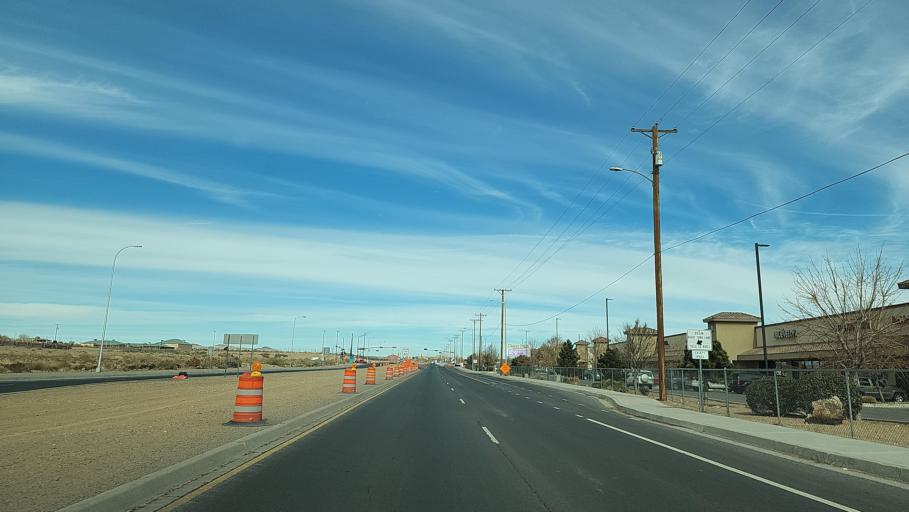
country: US
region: New Mexico
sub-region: Bernalillo County
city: Albuquerque
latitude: 35.0638
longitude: -106.7092
